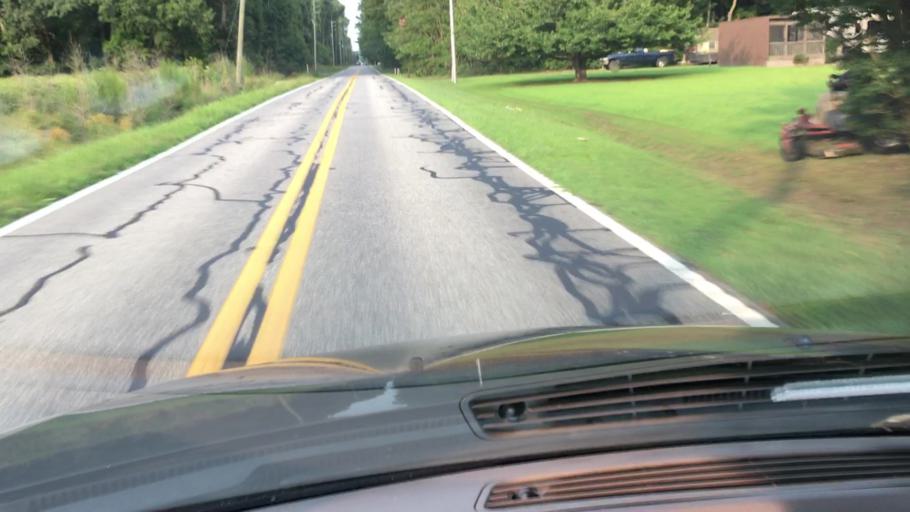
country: US
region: Delaware
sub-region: Sussex County
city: Ocean View
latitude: 38.5143
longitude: -75.0919
